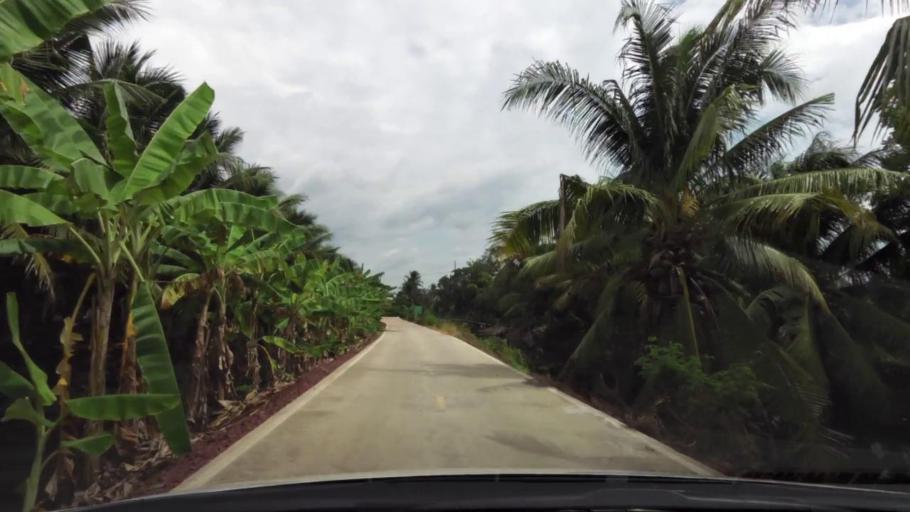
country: TH
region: Ratchaburi
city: Damnoen Saduak
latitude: 13.5557
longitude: 99.9806
